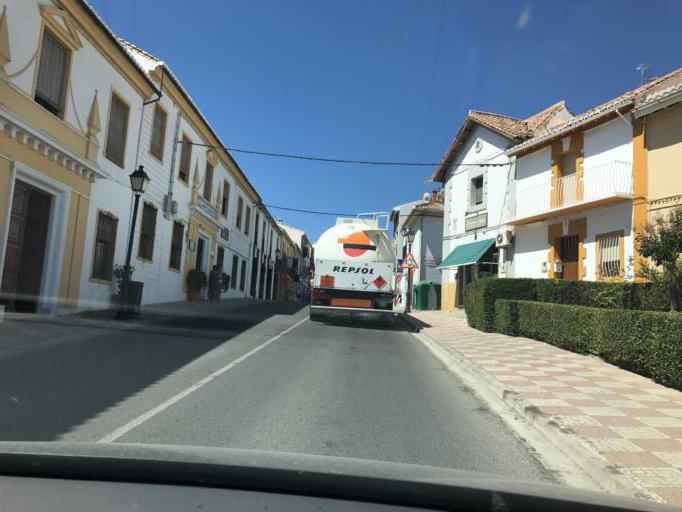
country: ES
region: Andalusia
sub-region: Provincia de Granada
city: Alhama de Granada
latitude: 37.0048
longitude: -3.9899
